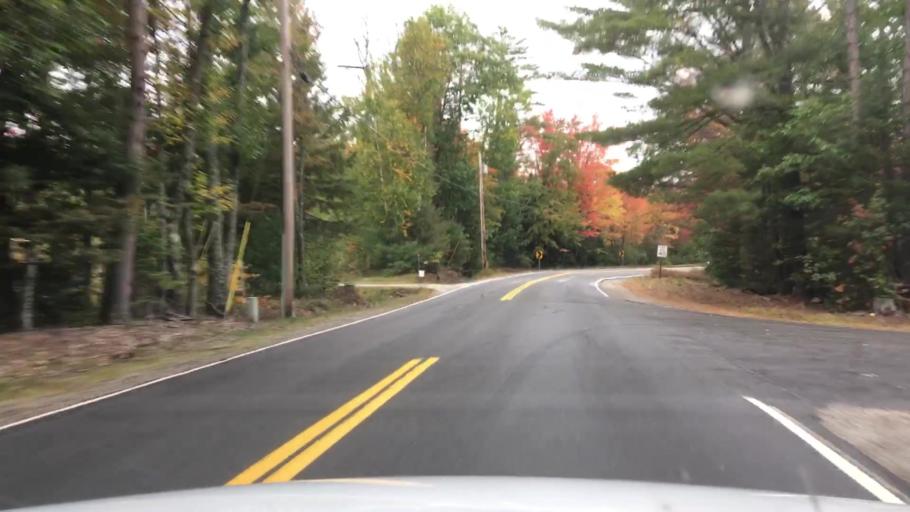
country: US
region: Maine
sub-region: Oxford County
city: Bethel
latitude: 44.3673
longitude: -70.7994
